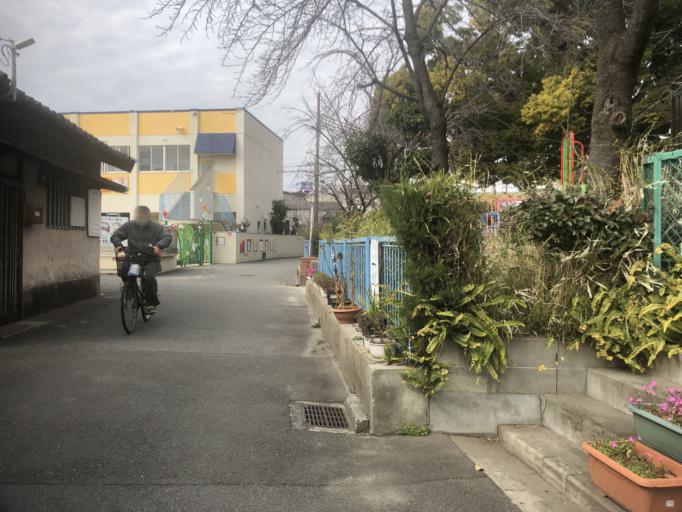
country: JP
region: Osaka
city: Daitocho
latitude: 34.6774
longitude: 135.5783
